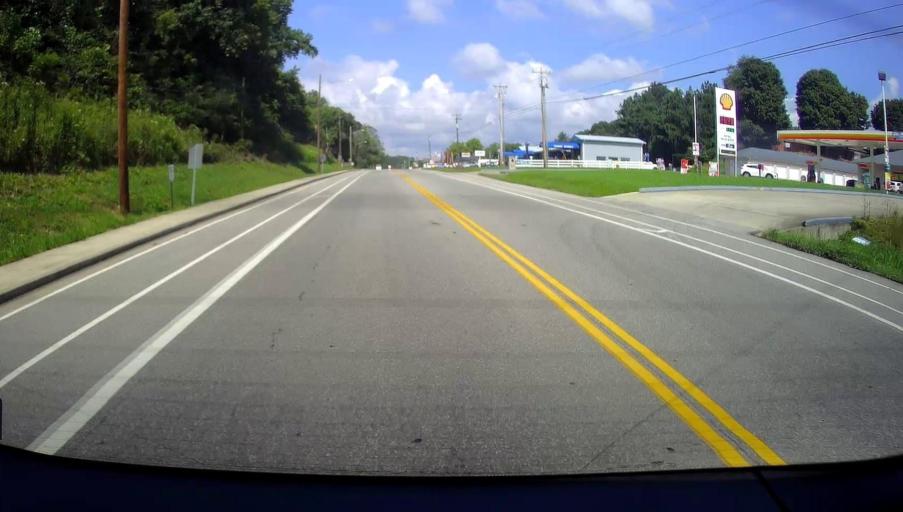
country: US
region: Tennessee
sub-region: Coffee County
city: Manchester
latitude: 35.4900
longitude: -86.0955
